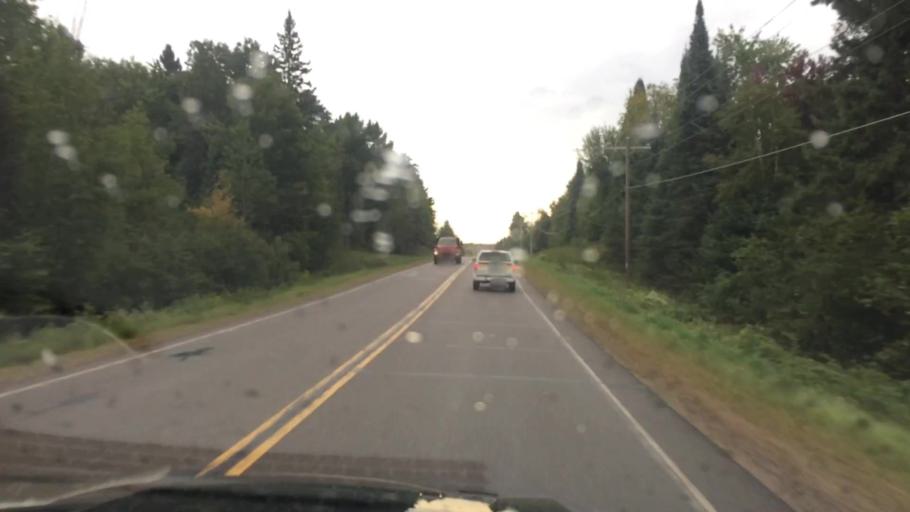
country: US
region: Wisconsin
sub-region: Lincoln County
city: Tomahawk
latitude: 45.4962
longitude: -89.7137
